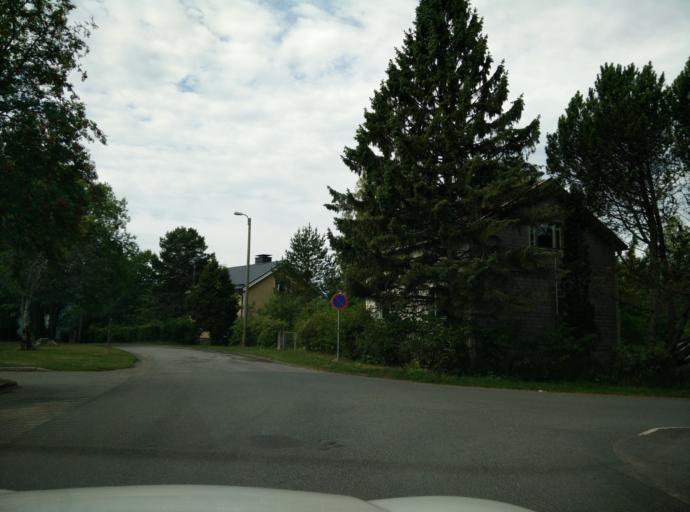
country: FI
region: Haeme
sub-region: Haemeenlinna
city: Haemeenlinna
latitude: 60.9887
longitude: 24.4476
